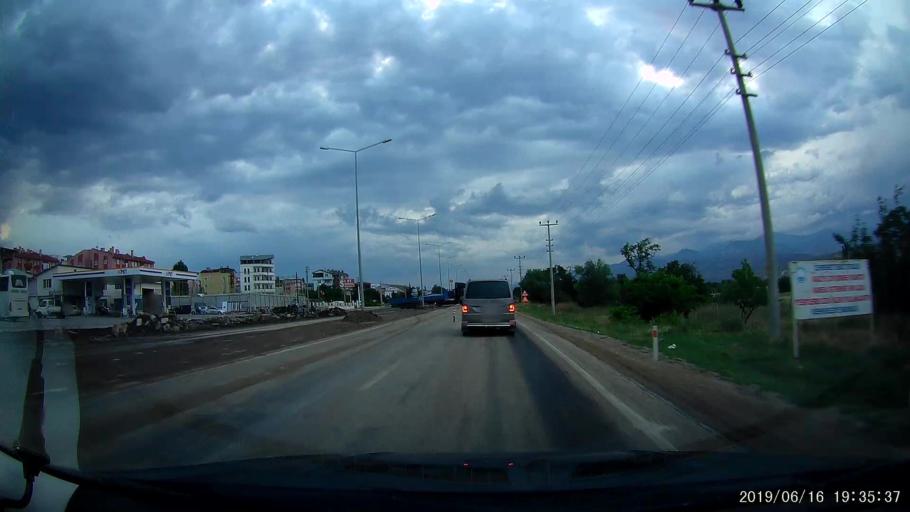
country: TR
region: Sivas
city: Susehri
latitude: 40.1711
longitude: 38.0915
